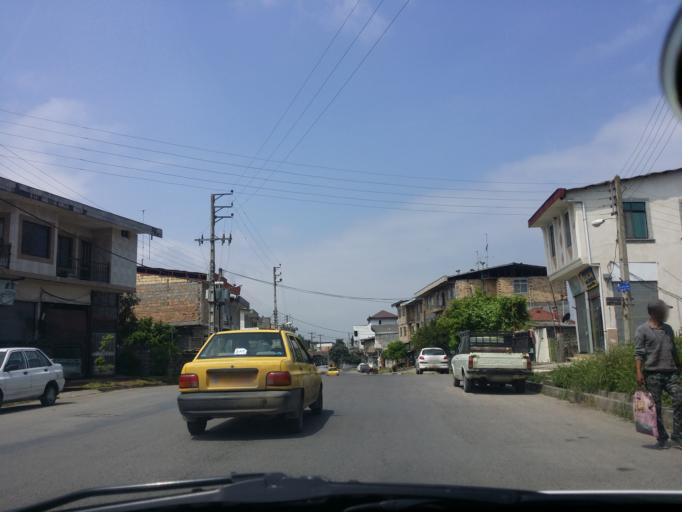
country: IR
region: Mazandaran
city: Chalus
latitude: 36.6702
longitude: 51.4031
